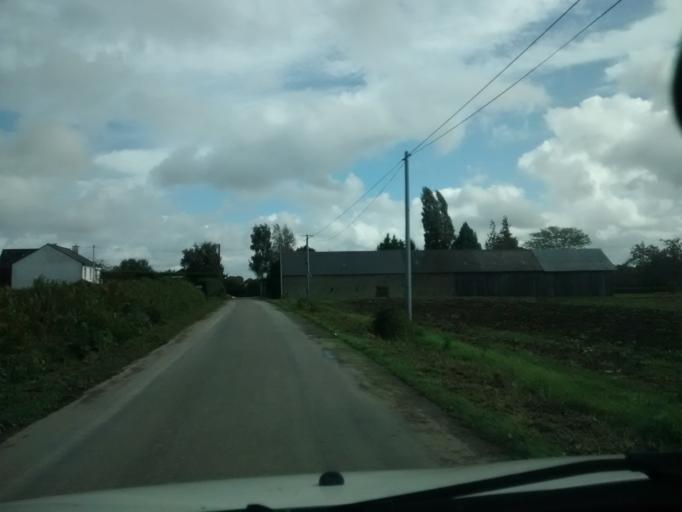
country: FR
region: Brittany
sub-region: Departement d'Ille-et-Vilaine
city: Chateaubourg
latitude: 48.1254
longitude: -1.3964
